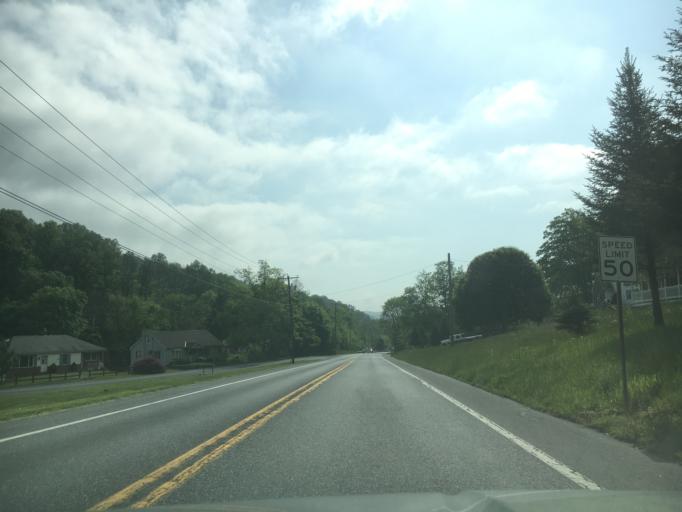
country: US
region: Pennsylvania
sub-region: Berks County
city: New Berlinville
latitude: 40.3623
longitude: -75.6848
